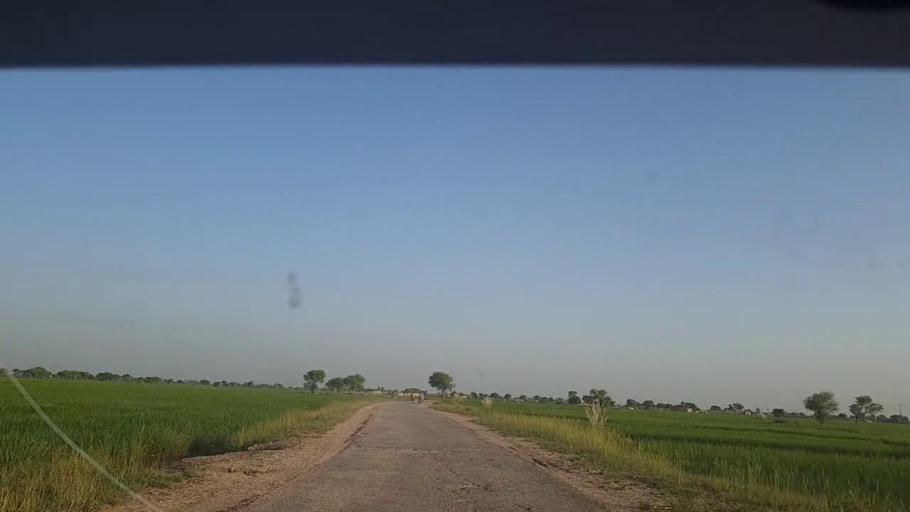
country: PK
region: Sindh
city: Thul
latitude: 28.1371
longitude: 68.8871
